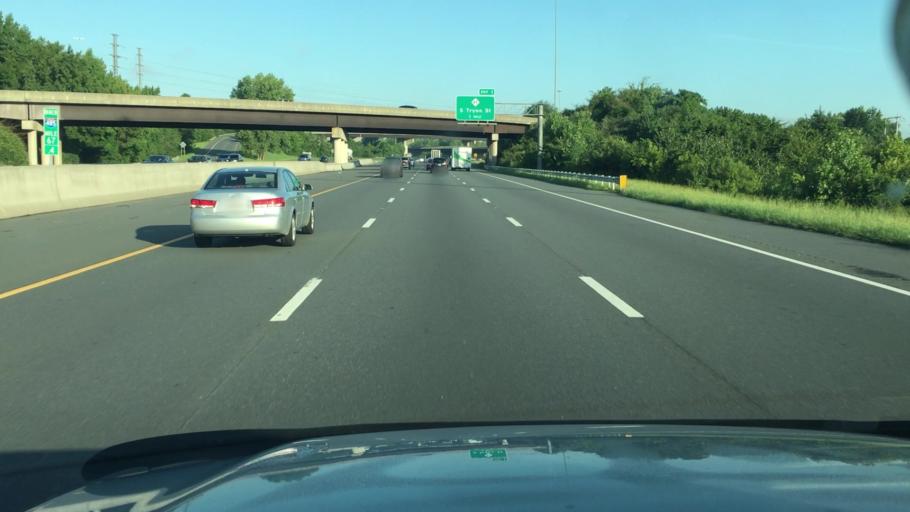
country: US
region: North Carolina
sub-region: Mecklenburg County
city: Pineville
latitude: 35.1229
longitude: -80.9114
